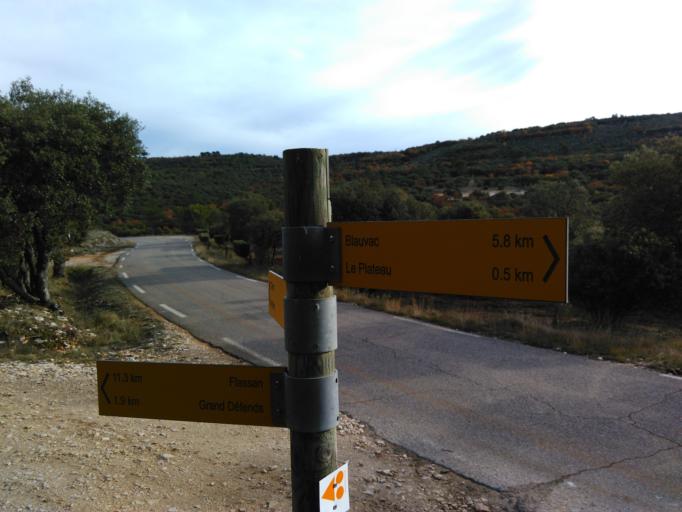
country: FR
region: Provence-Alpes-Cote d'Azur
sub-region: Departement du Vaucluse
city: Villes-sur-Auzon
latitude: 44.0427
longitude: 5.2514
